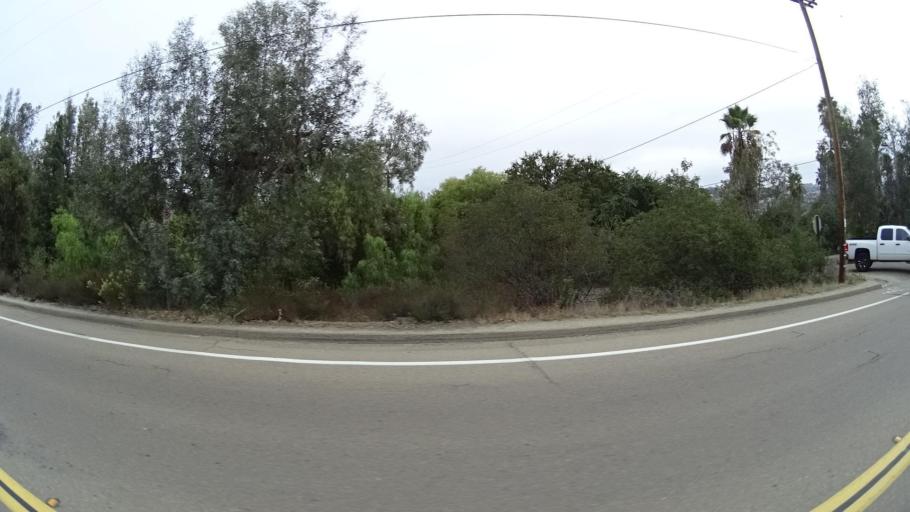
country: US
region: California
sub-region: San Diego County
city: Rancho San Diego
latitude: 32.7700
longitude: -116.9338
